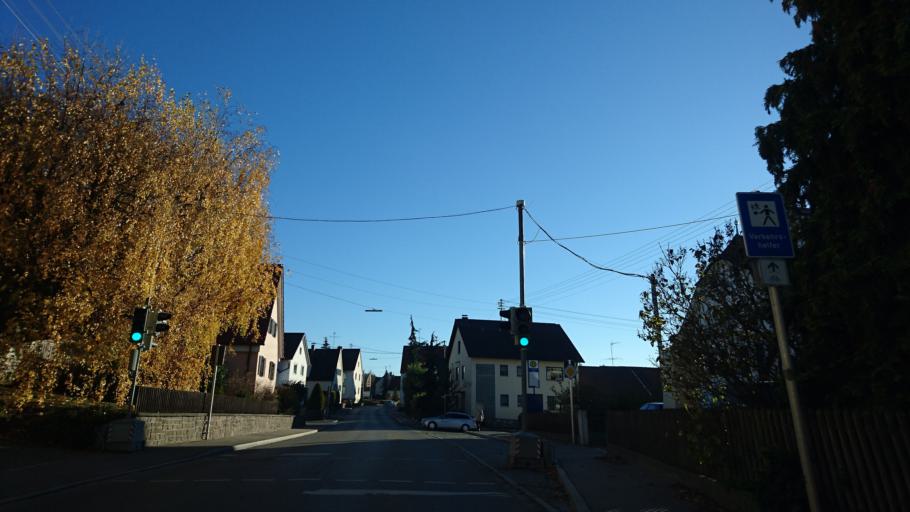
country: DE
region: Bavaria
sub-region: Swabia
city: Dinkelscherben
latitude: 48.3734
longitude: 10.5793
